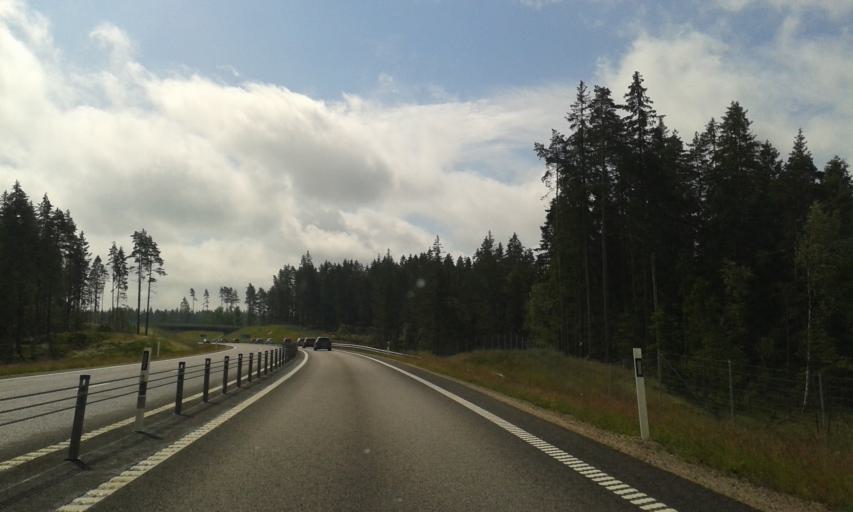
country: SE
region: Vaestra Goetaland
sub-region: Boras Kommun
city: Sjomarken
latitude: 57.7061
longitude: 12.8727
